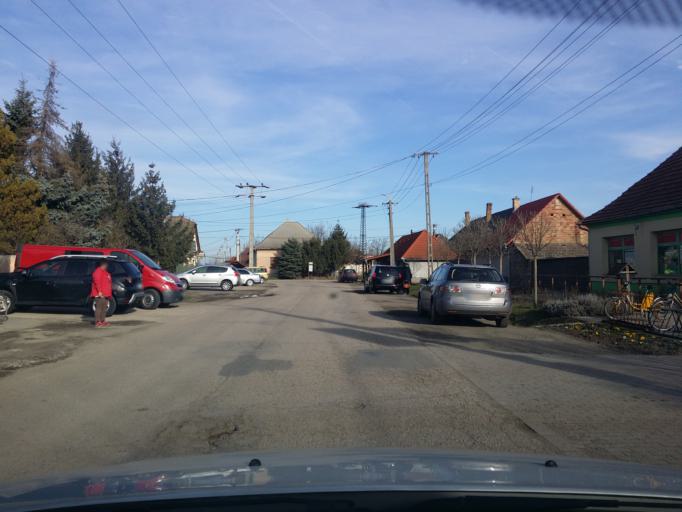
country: HU
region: Tolna
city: Madocsa
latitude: 46.6891
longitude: 18.9563
